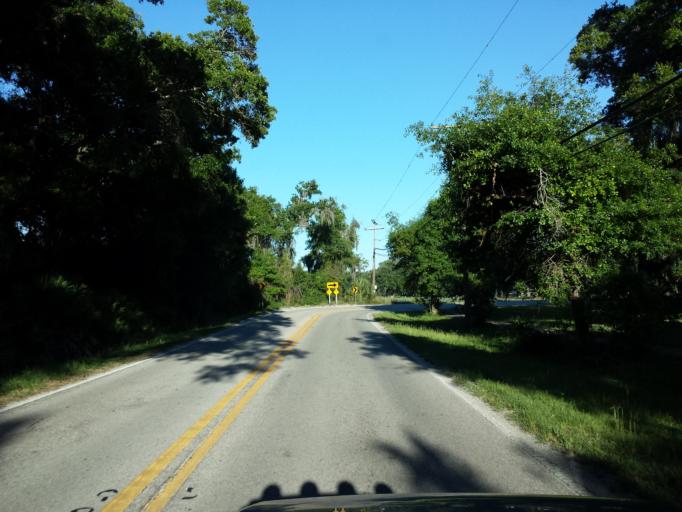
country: US
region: Florida
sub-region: Hillsborough County
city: Dover
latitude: 28.0325
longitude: -82.2455
